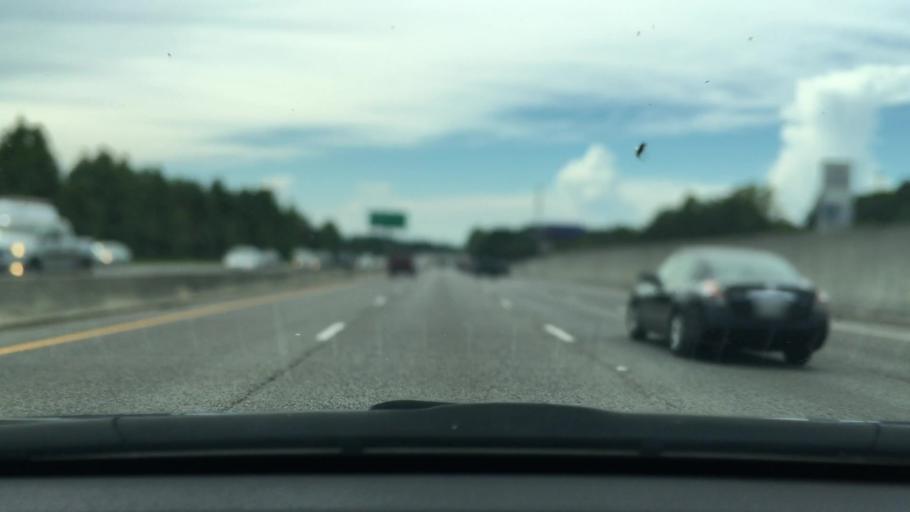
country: US
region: South Carolina
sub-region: Lexington County
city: West Columbia
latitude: 34.0143
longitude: -81.0818
